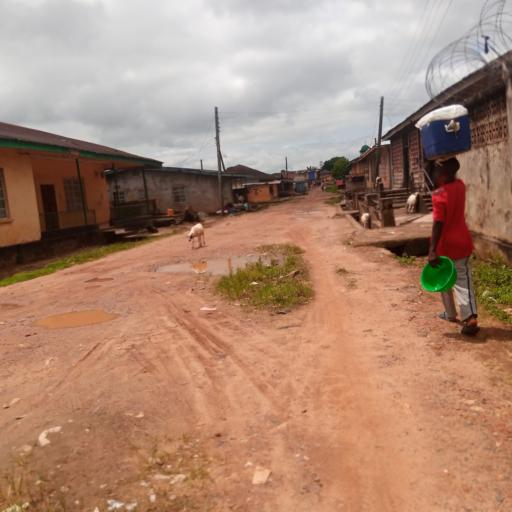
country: SL
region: Eastern Province
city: Kenema
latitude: 7.8884
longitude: -11.1870
